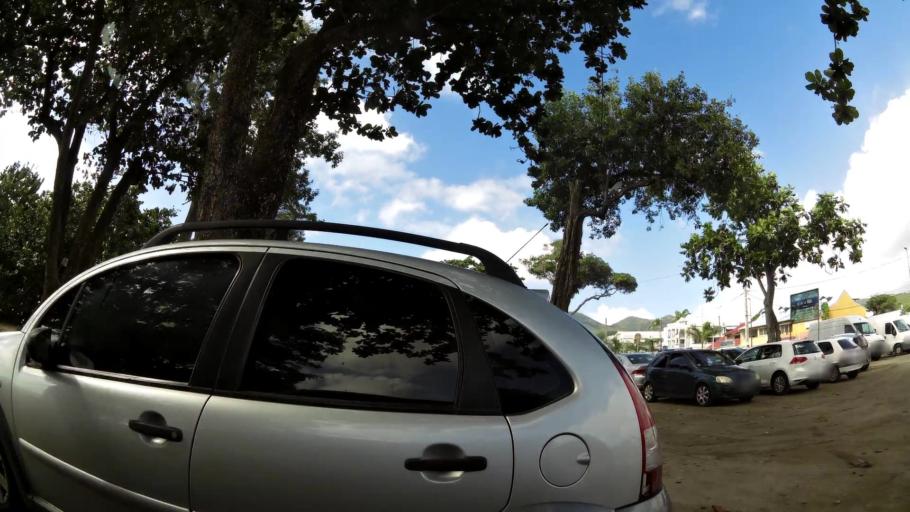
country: MQ
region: Martinique
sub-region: Martinique
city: Les Trois-Ilets
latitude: 14.4784
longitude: -61.0301
